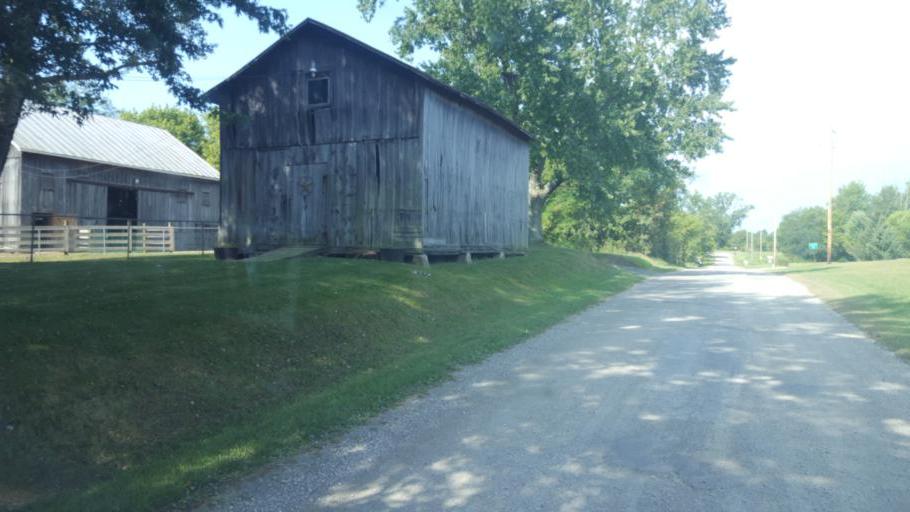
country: US
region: Ohio
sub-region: Morrow County
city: Cardington
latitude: 40.4833
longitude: -82.9602
